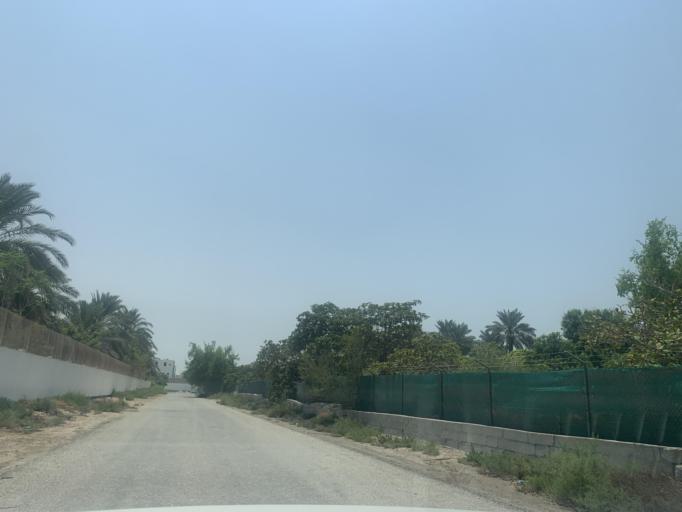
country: BH
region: Central Governorate
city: Madinat Hamad
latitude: 26.1490
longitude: 50.4623
